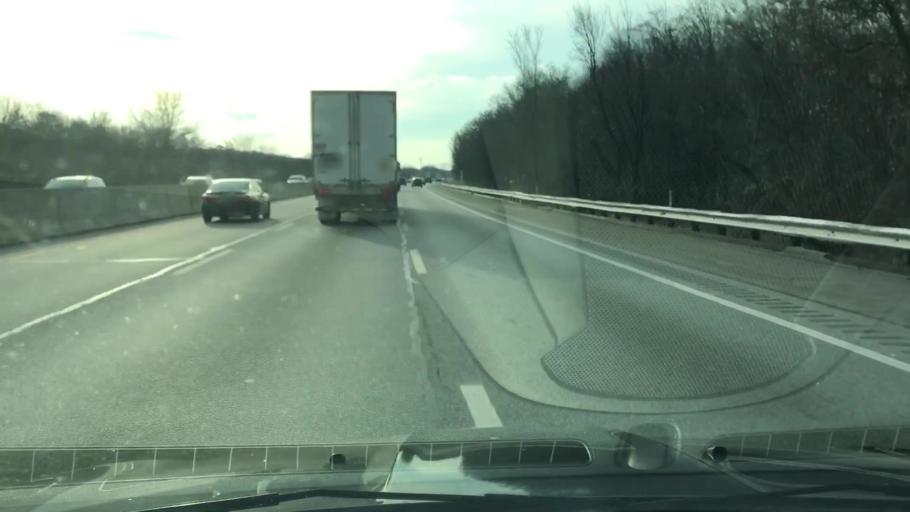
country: US
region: Pennsylvania
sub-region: Montgomery County
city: Dresher
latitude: 40.1438
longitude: -75.1585
